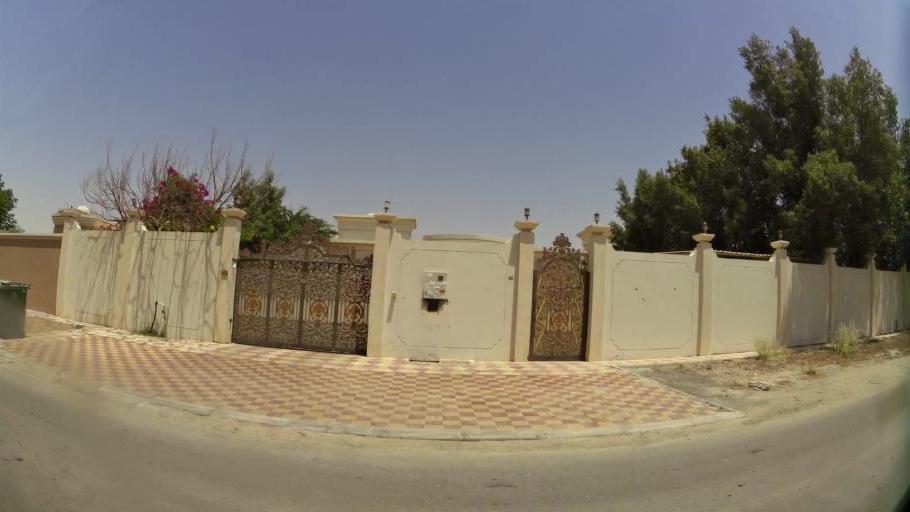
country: AE
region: Ajman
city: Ajman
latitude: 25.4200
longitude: 55.5050
